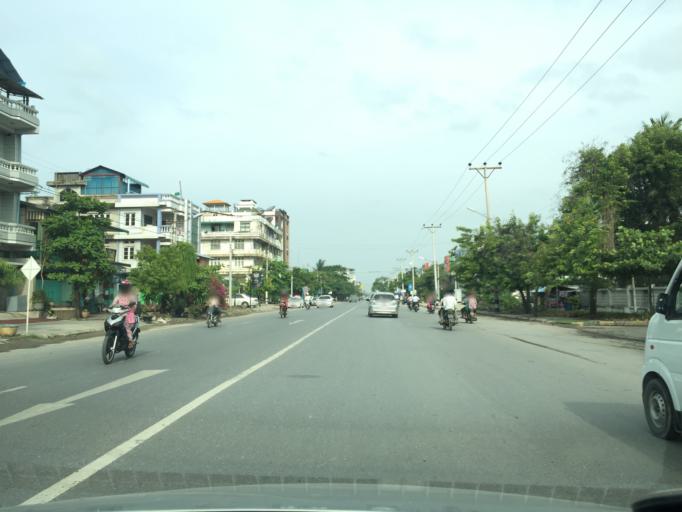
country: MM
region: Mandalay
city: Mandalay
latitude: 21.9682
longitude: 96.1009
